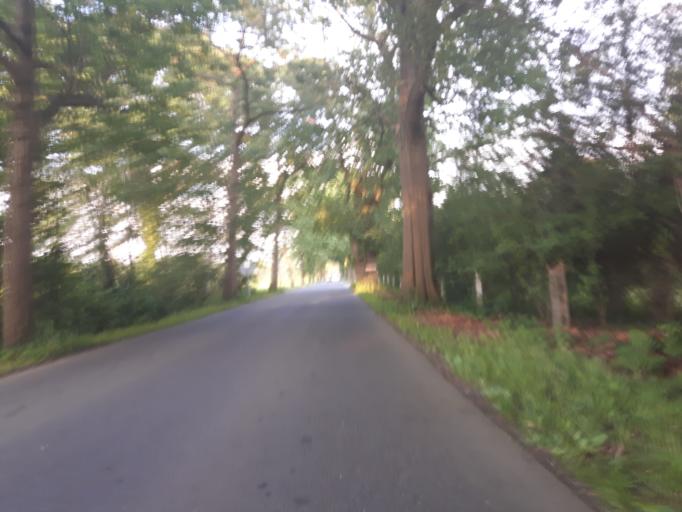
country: NL
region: Overijssel
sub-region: Gemeente Hengelo
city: Hengelo
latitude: 52.2414
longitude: 6.8163
